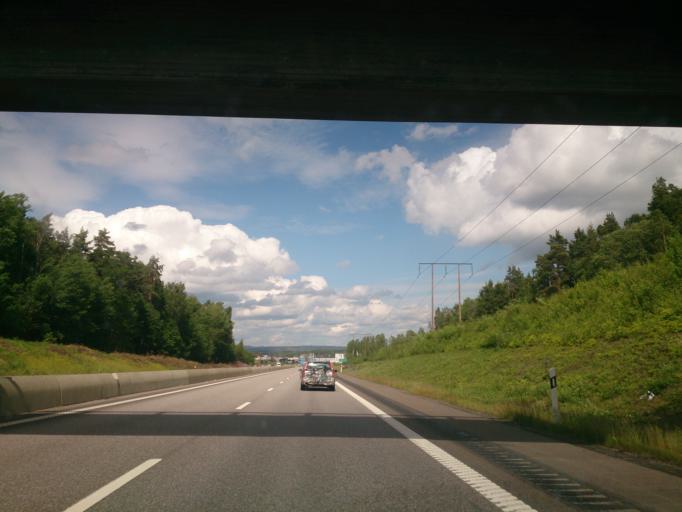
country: SE
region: OEstergoetland
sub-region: Norrkopings Kommun
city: Norrkoping
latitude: 58.6146
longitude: 16.1417
